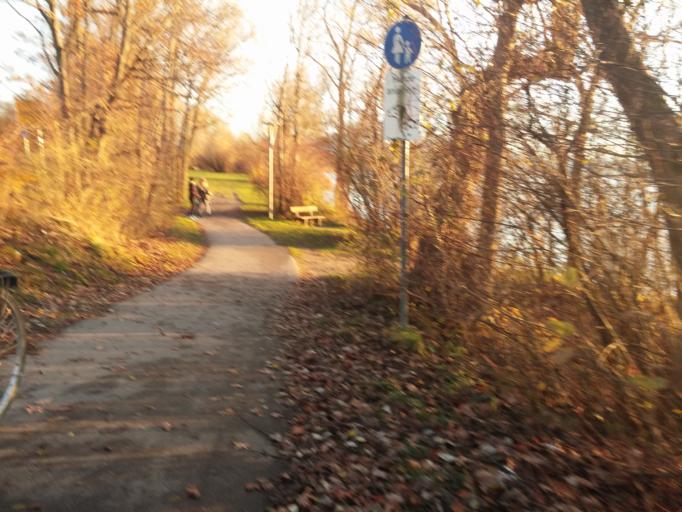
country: DE
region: Bavaria
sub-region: Upper Bavaria
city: Seeon-Seebruck
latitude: 47.9304
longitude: 12.4905
